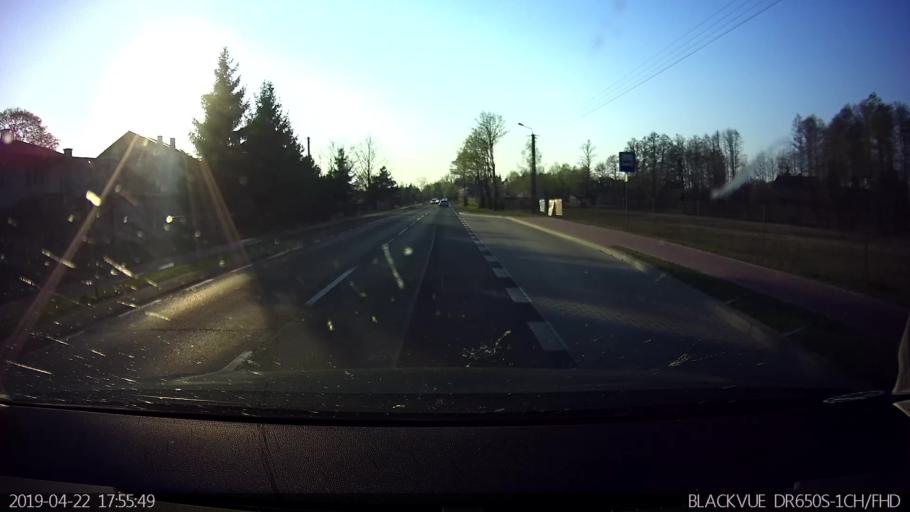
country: PL
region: Masovian Voivodeship
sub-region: Powiat wegrowski
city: Korytnica
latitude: 52.4630
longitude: 21.9148
